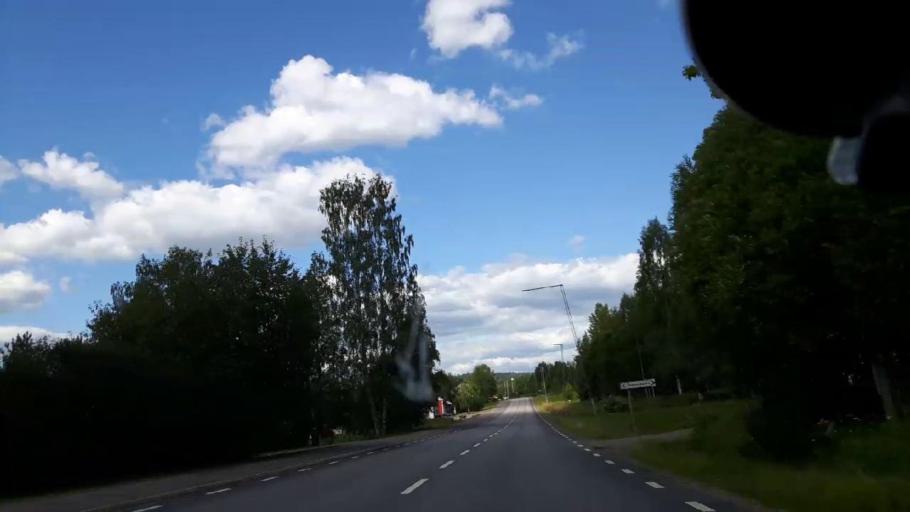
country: SE
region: Jaemtland
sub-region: Ragunda Kommun
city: Hammarstrand
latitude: 63.0065
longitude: 16.6670
